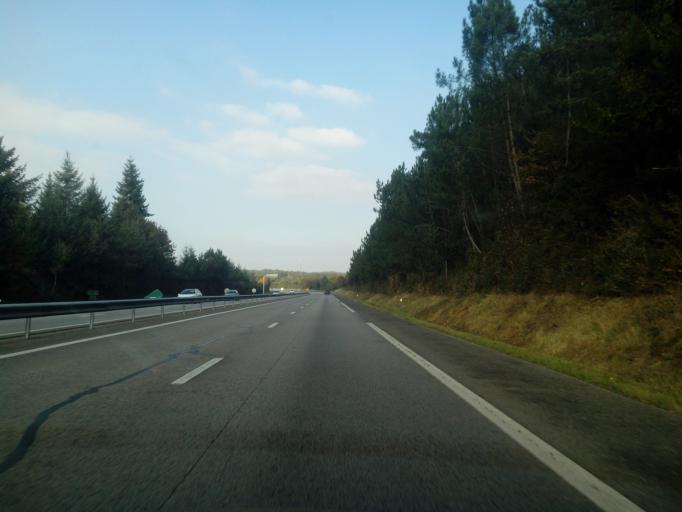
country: FR
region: Brittany
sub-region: Departement du Morbihan
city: Malestroit
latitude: 47.8002
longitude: -2.4469
